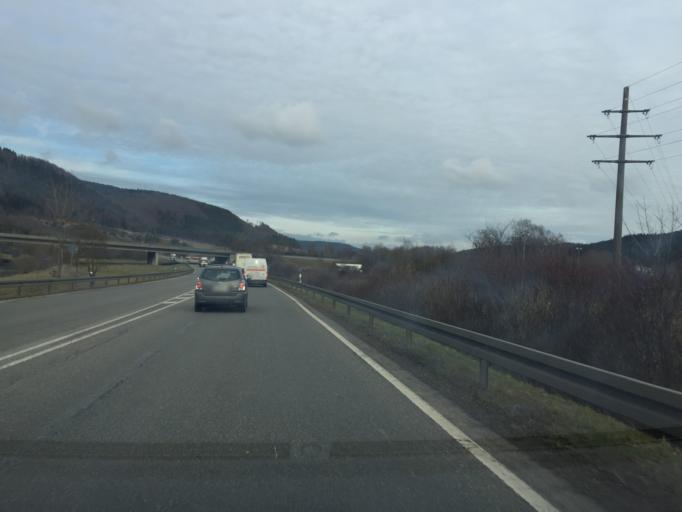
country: DE
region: Baden-Wuerttemberg
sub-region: Freiburg Region
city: Geisingen
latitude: 47.9195
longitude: 8.6692
